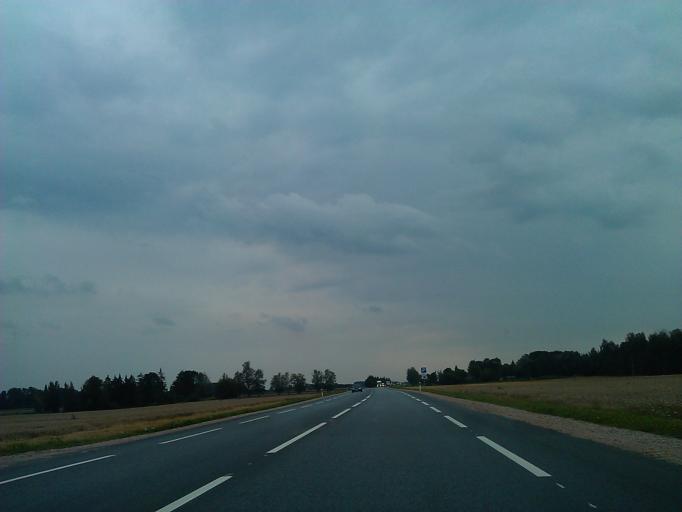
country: LV
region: Bauskas Rajons
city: Bauska
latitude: 56.4580
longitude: 24.1626
